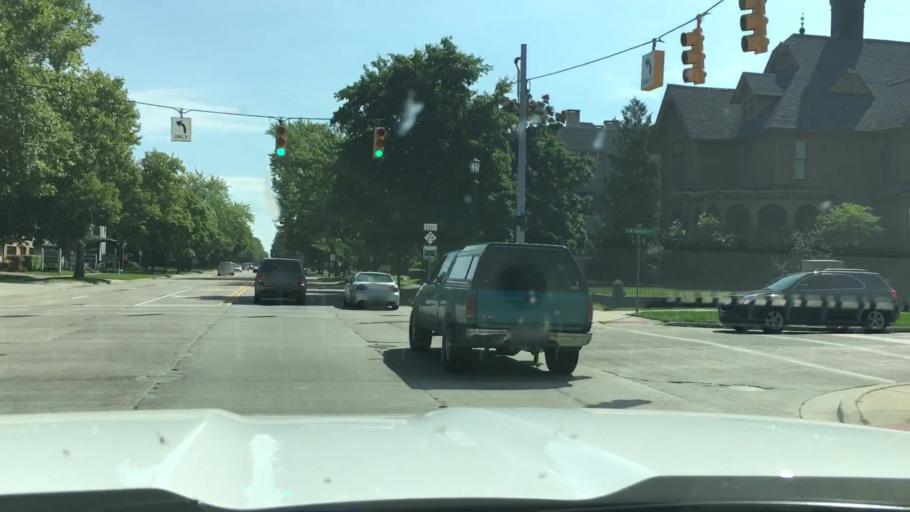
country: US
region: Michigan
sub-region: Bay County
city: Bay City
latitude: 43.5970
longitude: -83.8762
